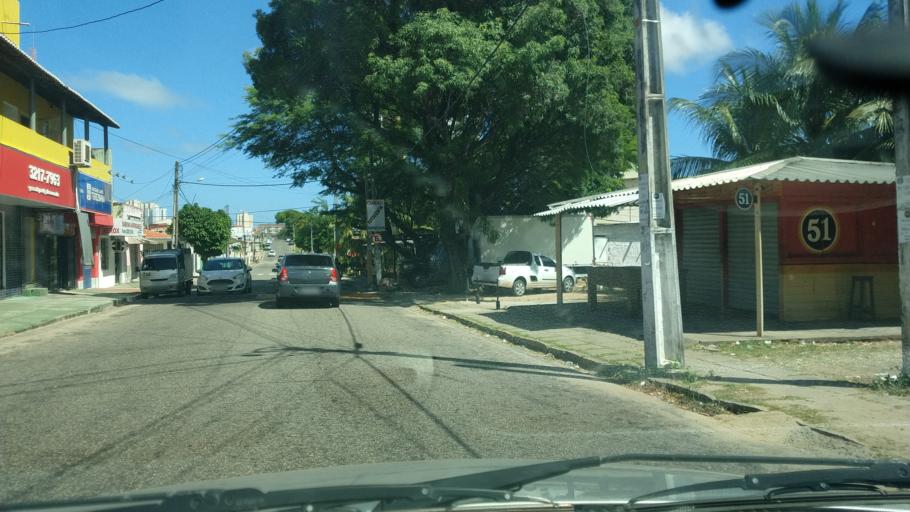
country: BR
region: Rio Grande do Norte
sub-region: Natal
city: Natal
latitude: -5.8579
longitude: -35.2107
